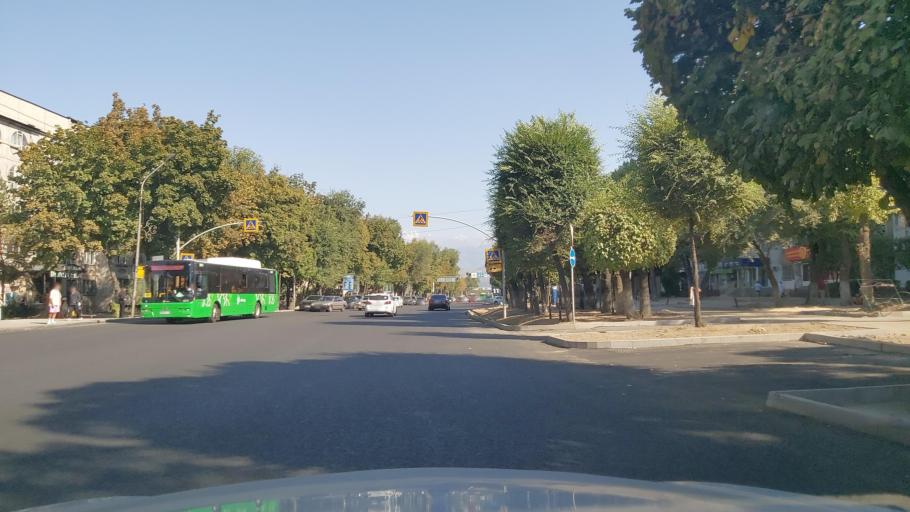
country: KZ
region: Almaty Oblysy
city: Pervomayskiy
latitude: 43.3239
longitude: 76.9103
